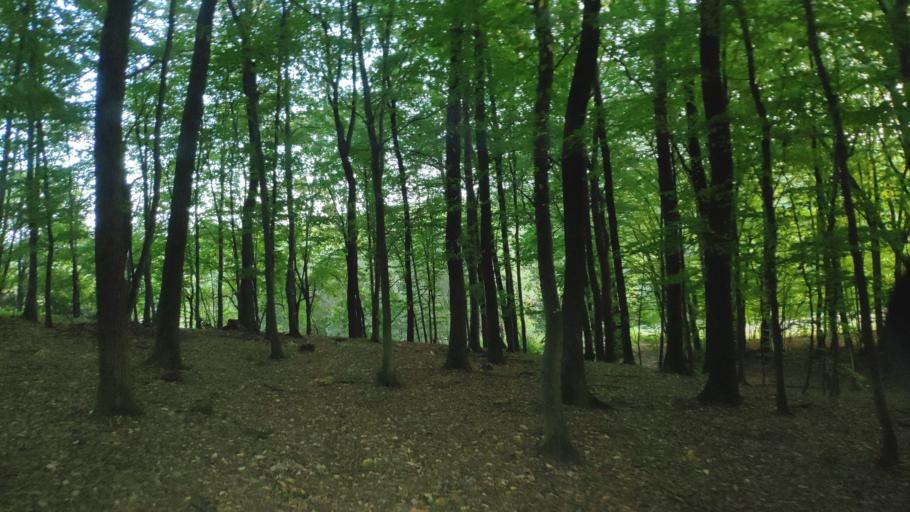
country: SK
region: Kosicky
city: Kosice
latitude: 48.7047
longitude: 21.1941
